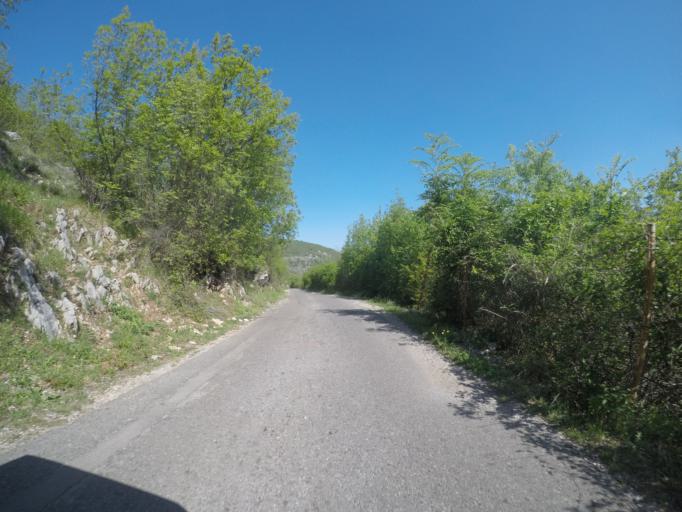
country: ME
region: Danilovgrad
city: Danilovgrad
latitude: 42.5284
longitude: 19.0933
